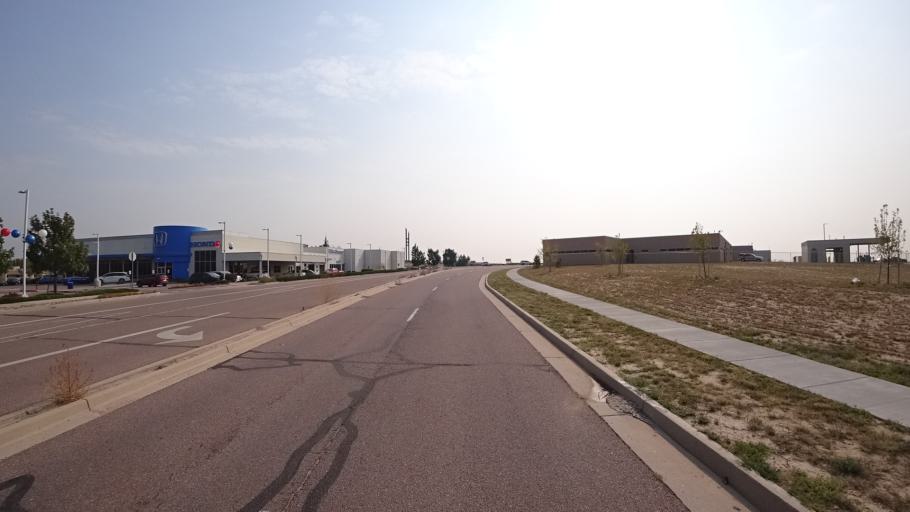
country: US
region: Colorado
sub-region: El Paso County
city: Stratmoor
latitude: 38.8169
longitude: -104.7555
